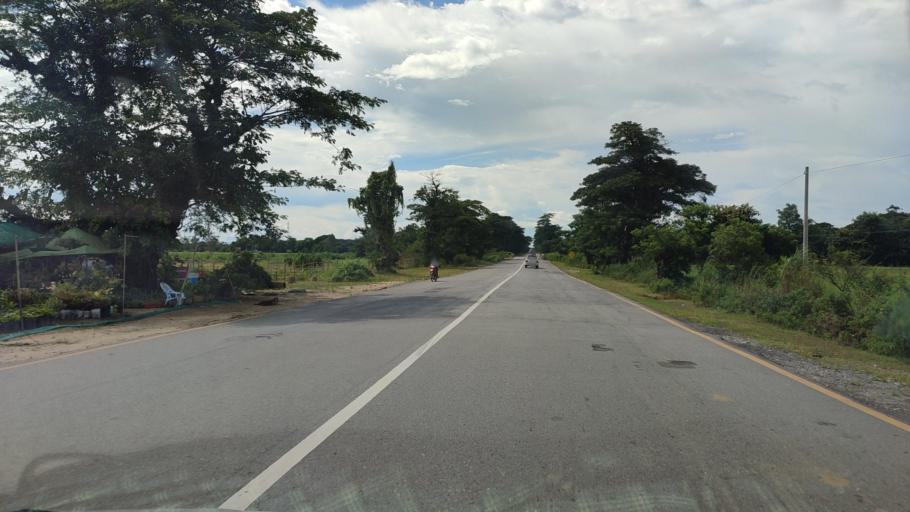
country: MM
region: Bago
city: Nyaunglebin
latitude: 18.1794
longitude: 96.5966
